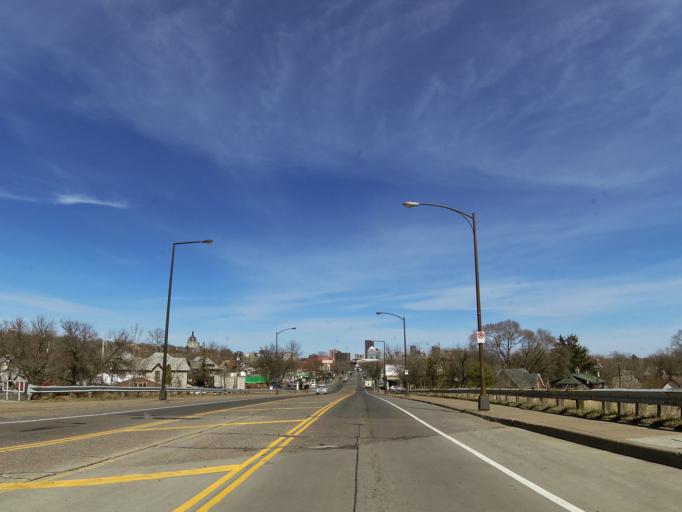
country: US
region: Minnesota
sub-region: Dakota County
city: West Saint Paul
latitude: 44.9327
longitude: -93.1193
